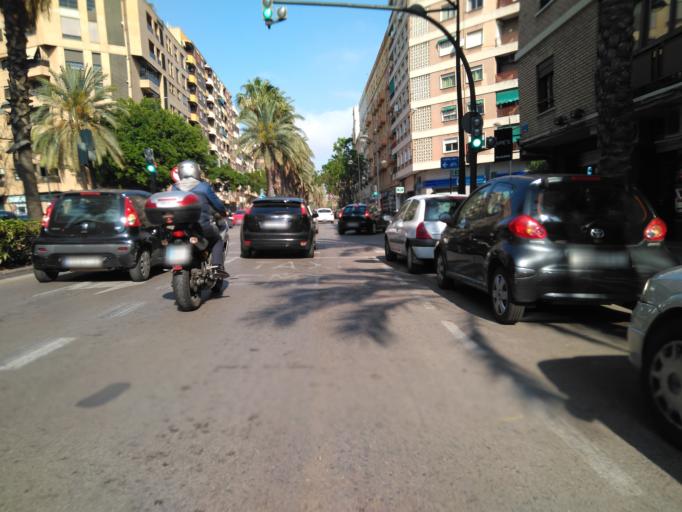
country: ES
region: Valencia
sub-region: Provincia de Valencia
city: Valencia
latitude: 39.4856
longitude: -0.3790
